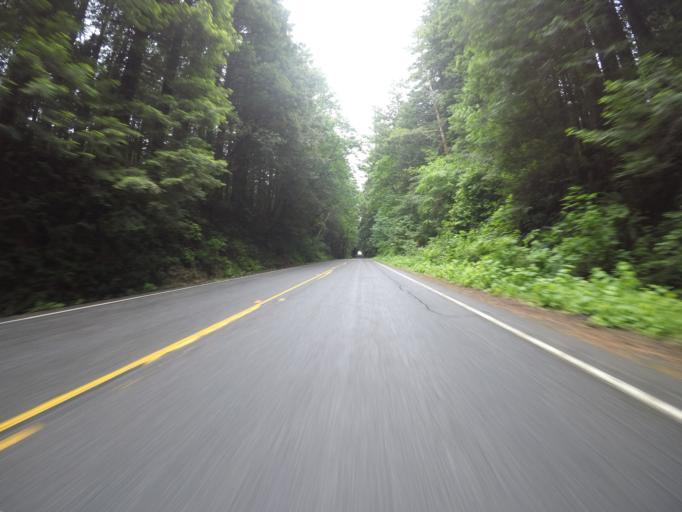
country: US
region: California
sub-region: Humboldt County
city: Rio Dell
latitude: 40.4463
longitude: -124.0104
